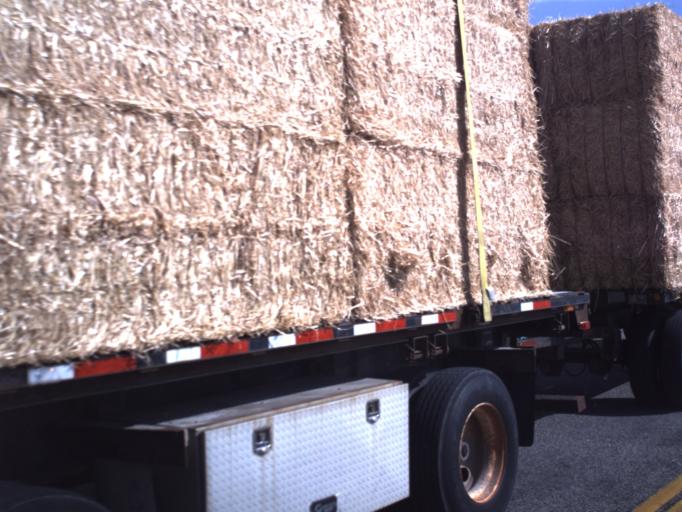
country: US
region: Utah
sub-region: Box Elder County
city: Garland
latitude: 41.7459
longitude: -112.0995
